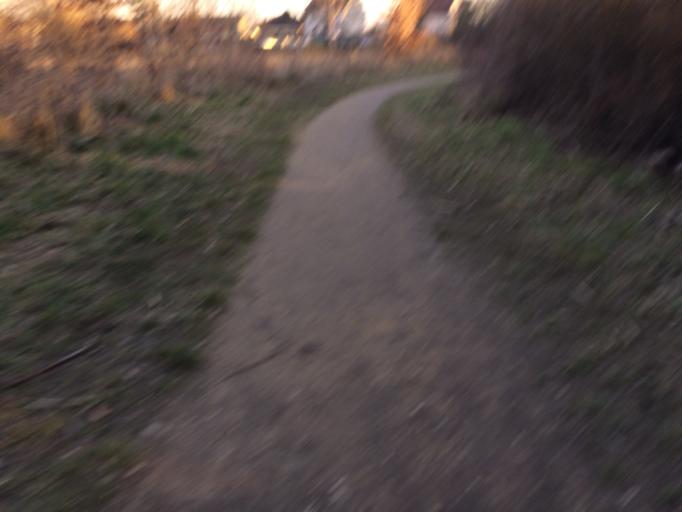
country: FR
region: Ile-de-France
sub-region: Departement de l'Essonne
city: Villebon-sur-Yvette
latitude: 48.7102
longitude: 2.2228
